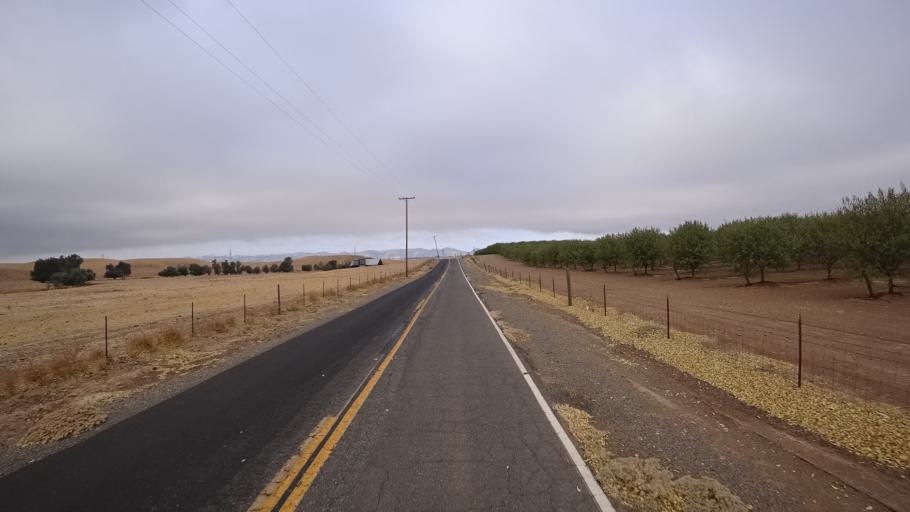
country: US
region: California
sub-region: Yolo County
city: Dunnigan
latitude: 38.8620
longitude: -122.0394
